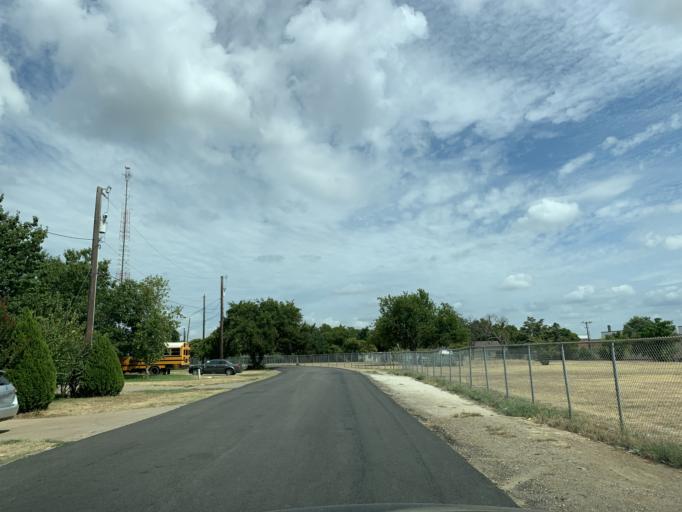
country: US
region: Texas
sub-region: Dallas County
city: Cockrell Hill
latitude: 32.7614
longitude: -96.8671
